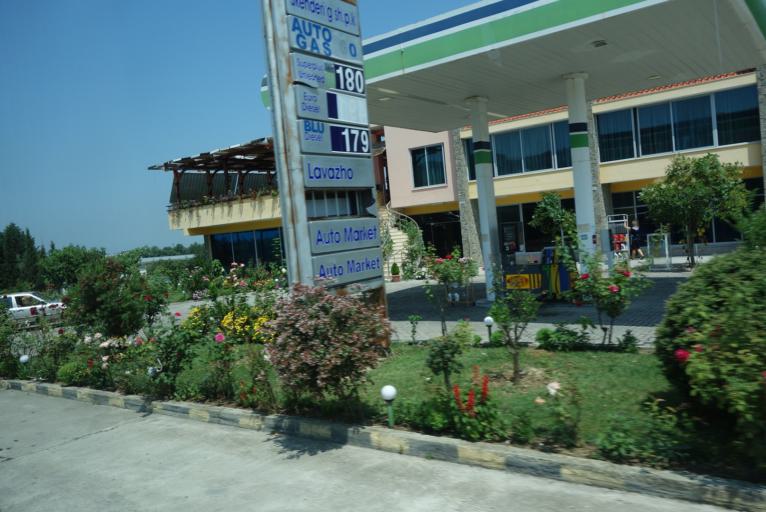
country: AL
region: Tirane
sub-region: Rrethi i Tiranes
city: Ndroq
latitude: 41.2728
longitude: 19.6230
